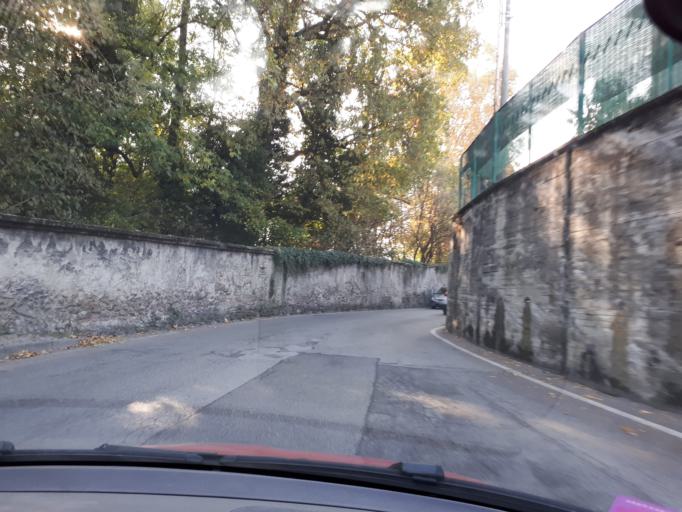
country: IT
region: Lombardy
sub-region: Provincia di Monza e Brianza
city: Biassono
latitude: 45.6292
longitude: 9.2778
